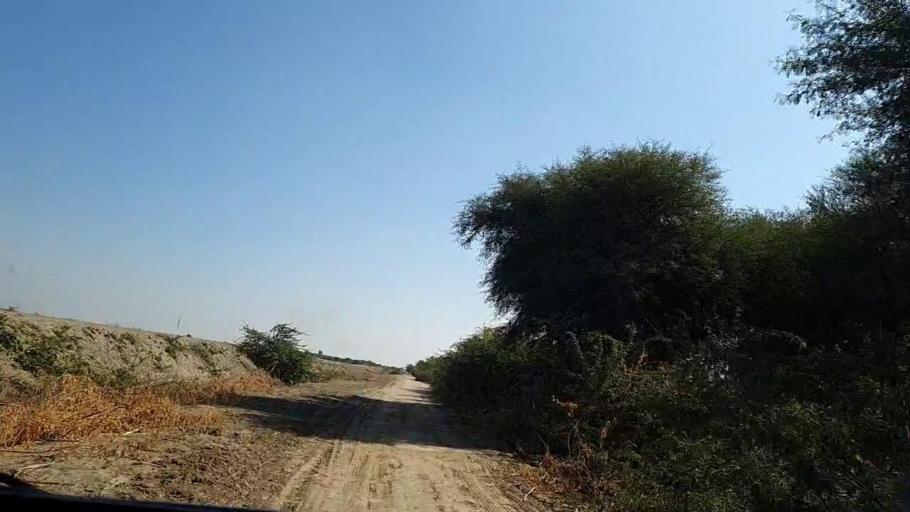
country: PK
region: Sindh
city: Tando Mittha Khan
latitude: 25.7671
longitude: 69.3026
